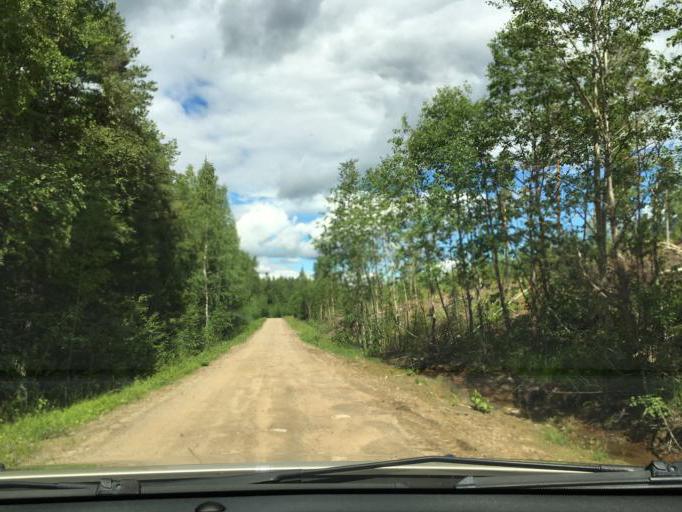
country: SE
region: Norrbotten
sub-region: Overkalix Kommun
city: OEverkalix
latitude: 66.1615
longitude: 22.8549
